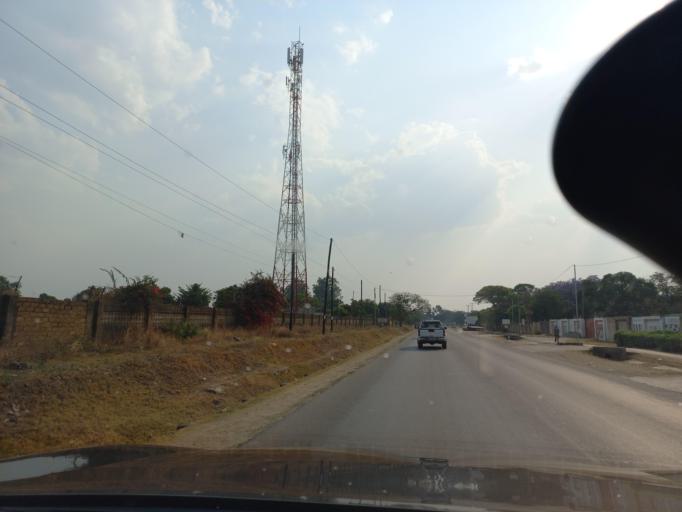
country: ZM
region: Lusaka
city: Lusaka
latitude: -15.4610
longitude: 28.2502
